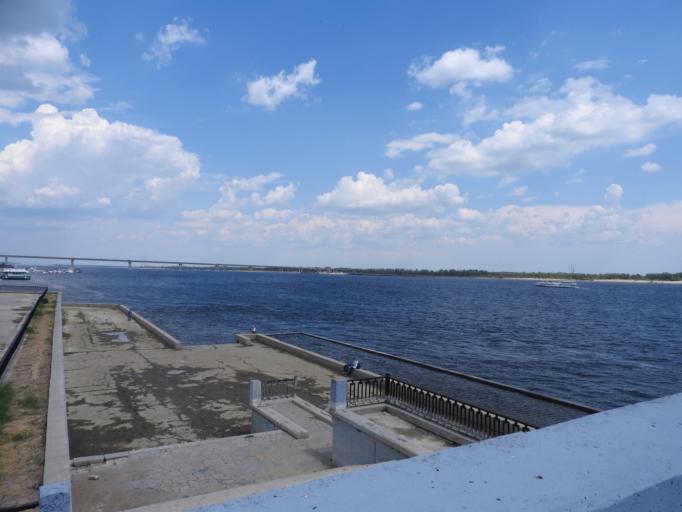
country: RU
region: Volgograd
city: Volgograd
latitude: 48.7115
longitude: 44.5339
